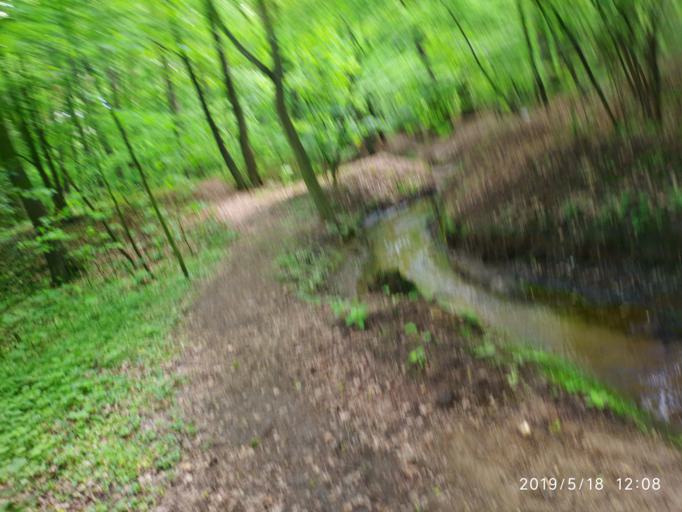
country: PL
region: Lubusz
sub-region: Zielona Gora
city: Zielona Gora
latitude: 51.9470
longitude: 15.5421
